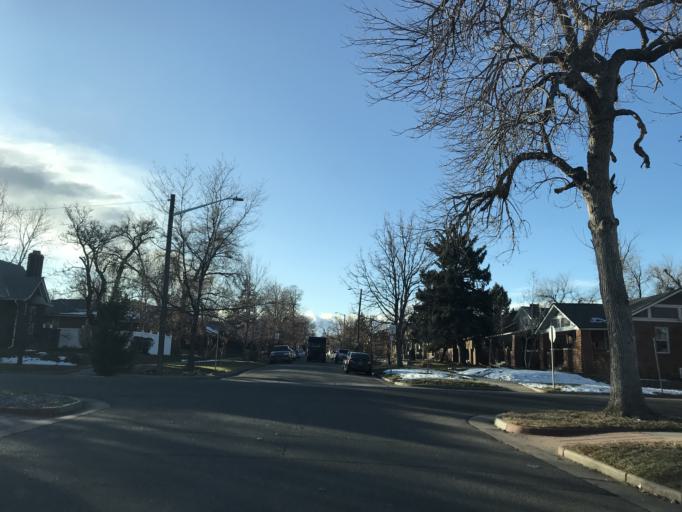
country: US
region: Colorado
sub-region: Denver County
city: Denver
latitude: 39.7660
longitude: -104.9635
